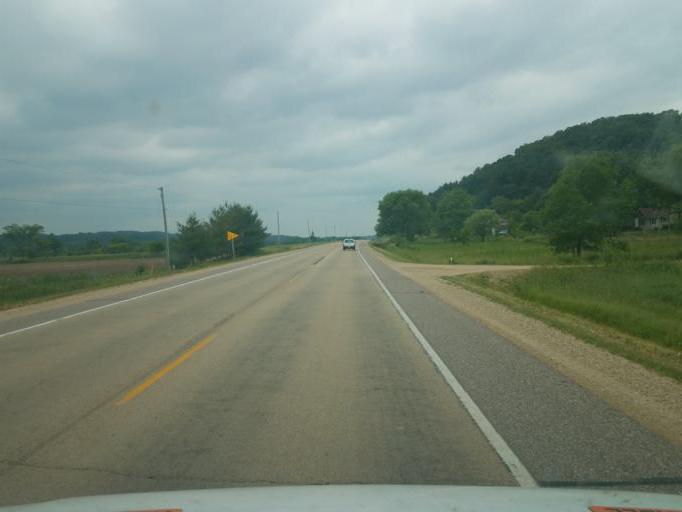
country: US
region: Wisconsin
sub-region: Juneau County
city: Elroy
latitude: 43.6189
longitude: -90.1517
